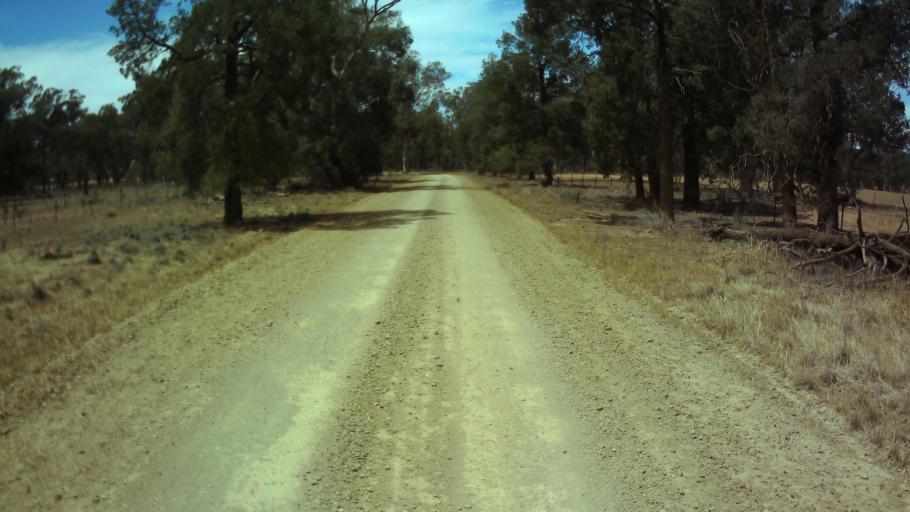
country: AU
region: New South Wales
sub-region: Weddin
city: Grenfell
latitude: -33.8560
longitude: 147.8052
